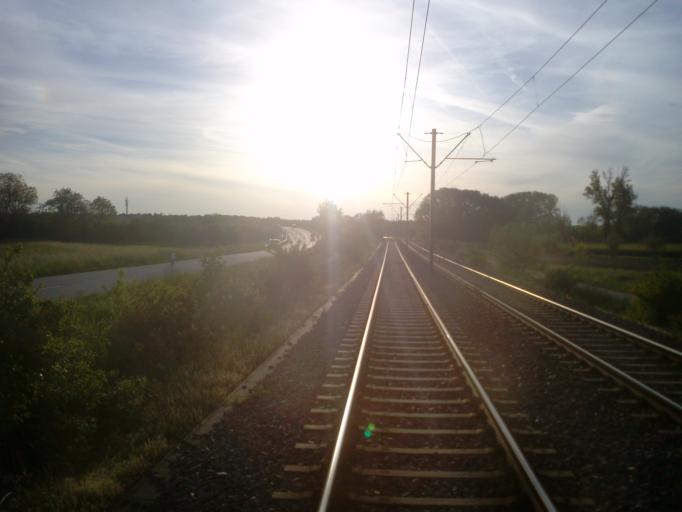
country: DE
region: Baden-Wuerttemberg
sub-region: Karlsruhe Region
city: Karlsdorf-Neuthard
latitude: 49.1139
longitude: 8.4847
